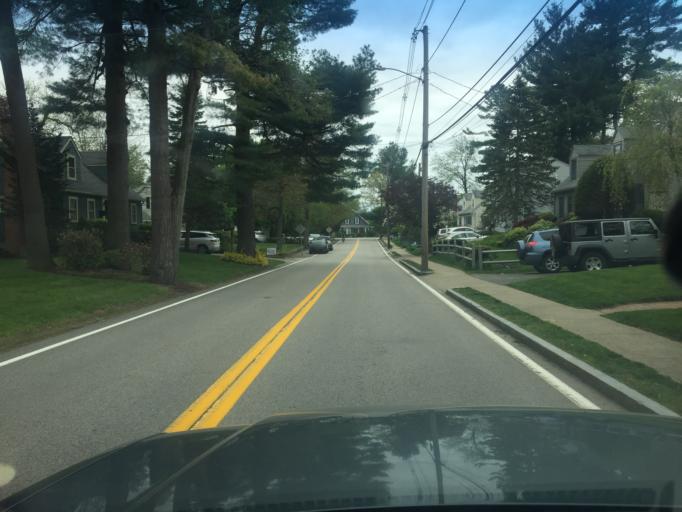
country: US
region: Massachusetts
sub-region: Norfolk County
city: Norwood
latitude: 42.2198
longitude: -71.1916
